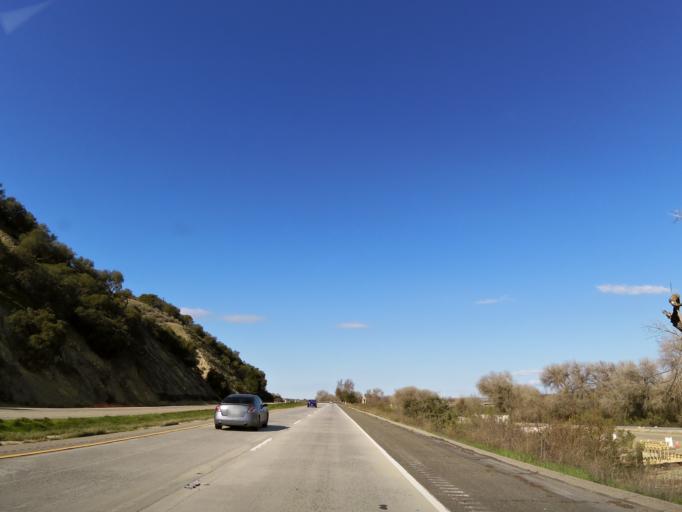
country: US
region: California
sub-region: San Luis Obispo County
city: Lake Nacimiento
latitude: 35.9578
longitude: -120.8826
